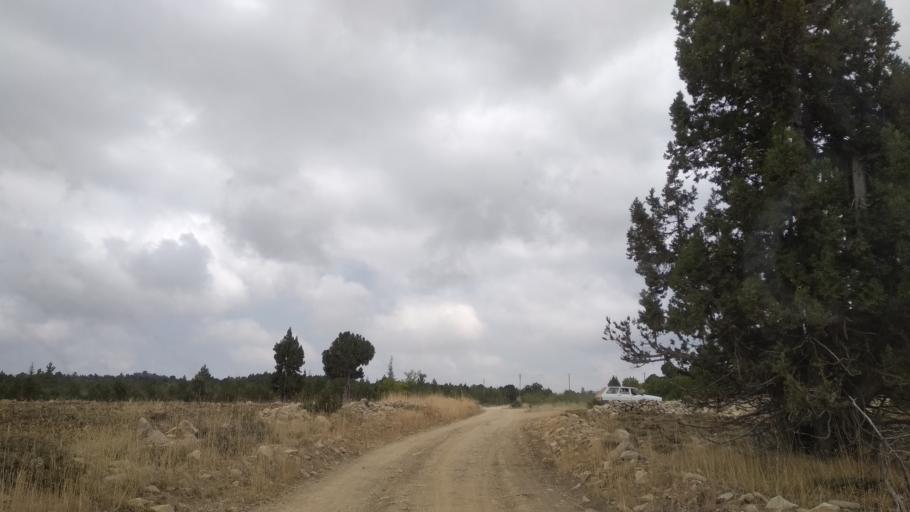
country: TR
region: Mersin
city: Sarikavak
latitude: 36.5666
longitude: 33.7656
